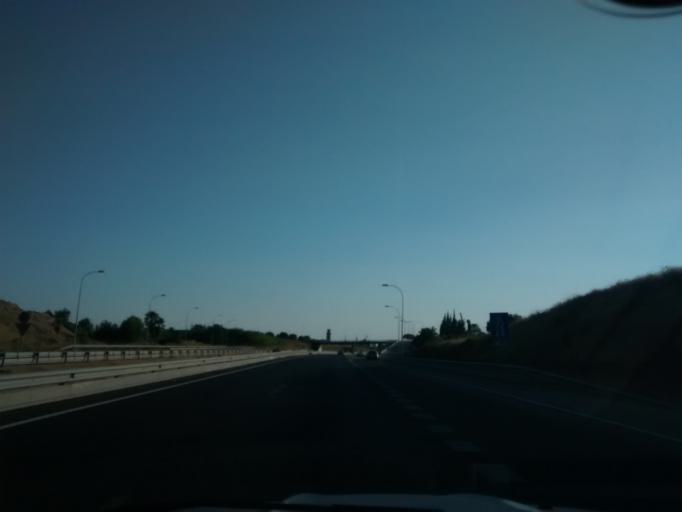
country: ES
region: Balearic Islands
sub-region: Illes Balears
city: Campanet
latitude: 39.7697
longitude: 2.9754
